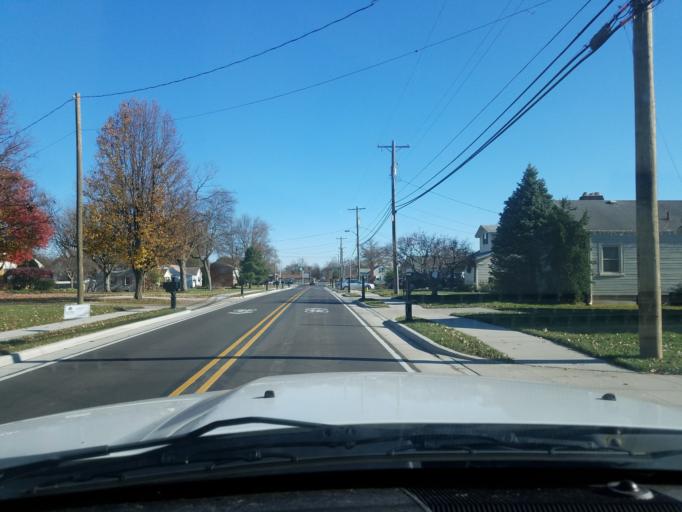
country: US
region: Indiana
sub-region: Floyd County
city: New Albany
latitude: 38.3179
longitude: -85.8065
